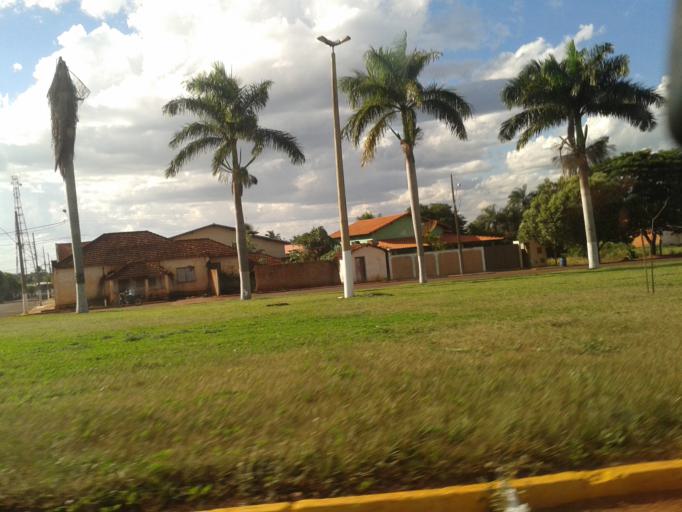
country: BR
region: Minas Gerais
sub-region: Santa Vitoria
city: Santa Vitoria
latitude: -18.6967
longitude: -49.9407
